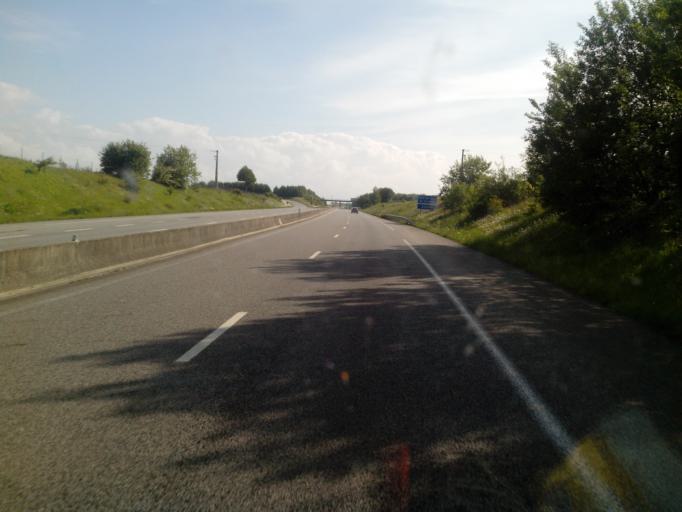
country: FR
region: Haute-Normandie
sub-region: Departement de la Seine-Maritime
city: Foucarmont
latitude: 49.8357
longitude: 1.5292
